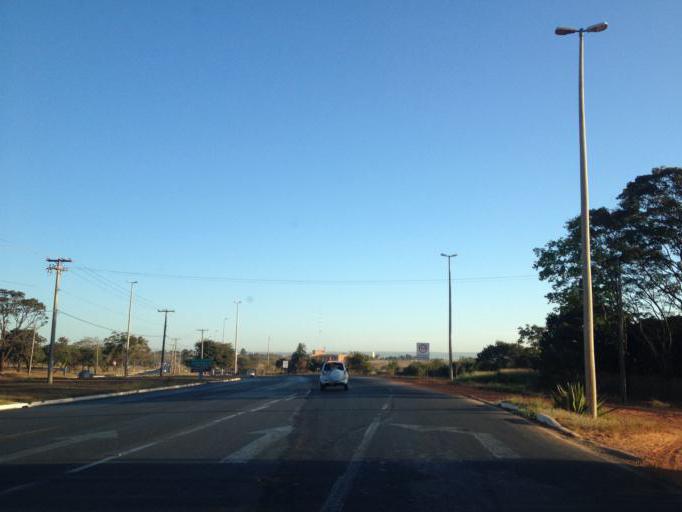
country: BR
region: Federal District
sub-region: Brasilia
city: Brasilia
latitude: -15.7713
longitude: -47.9097
